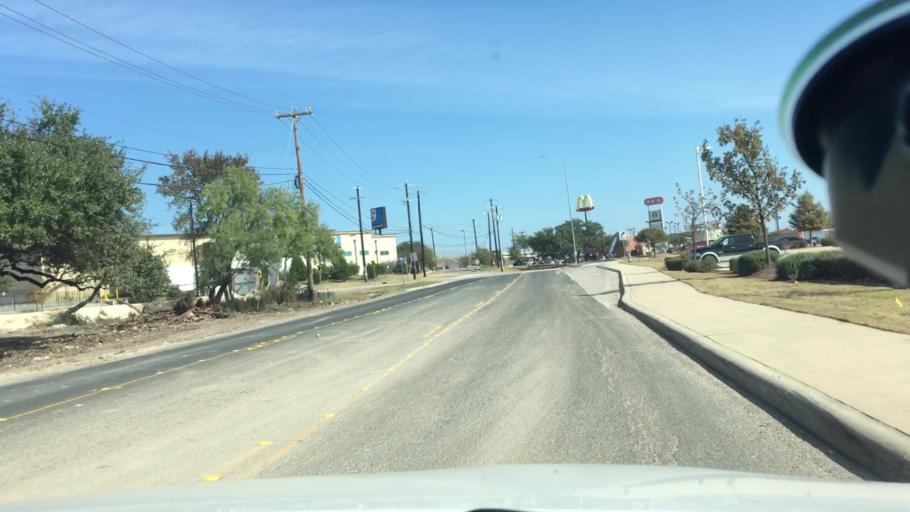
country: US
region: Texas
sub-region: Bexar County
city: Hollywood Park
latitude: 29.5984
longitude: -98.4215
